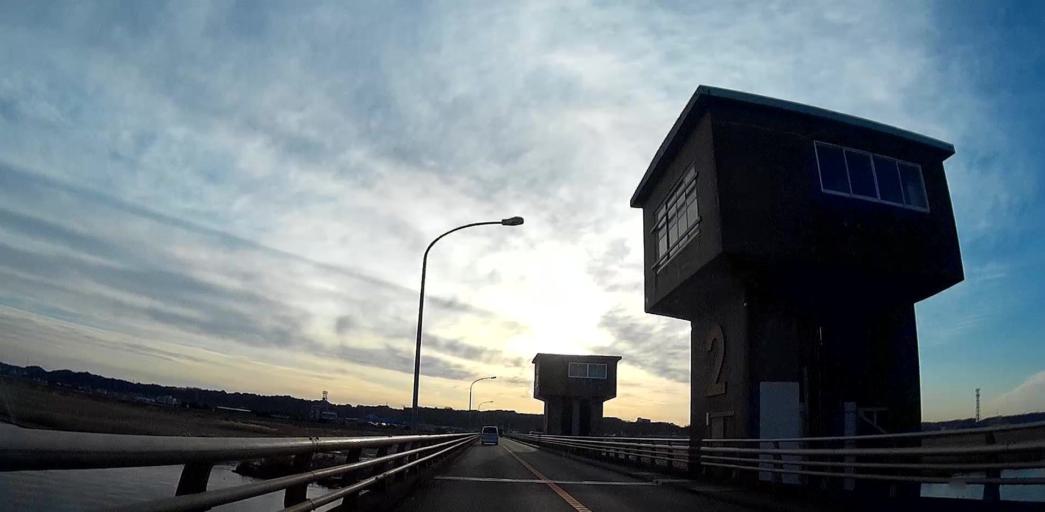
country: JP
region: Chiba
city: Omigawa
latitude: 35.8363
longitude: 140.7028
